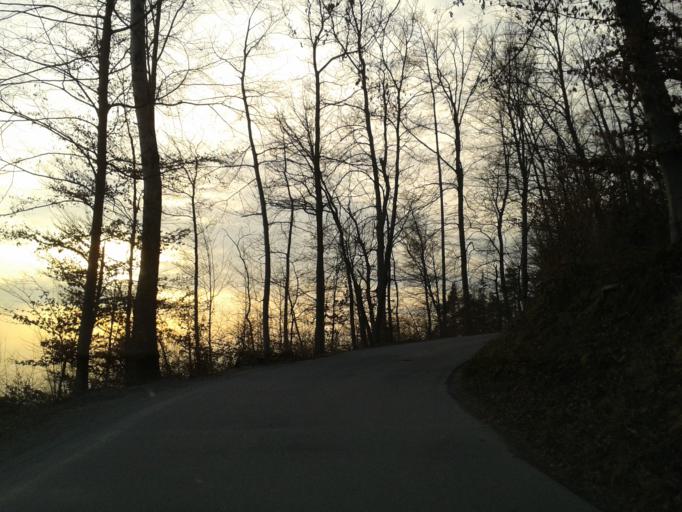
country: AT
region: Styria
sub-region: Politischer Bezirk Graz-Umgebung
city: Stattegg
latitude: 47.1380
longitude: 15.4401
